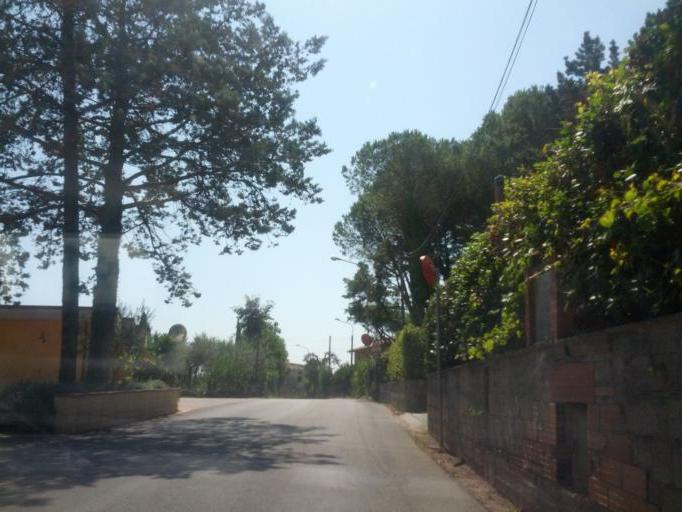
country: IT
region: Latium
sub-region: Provincia di Latina
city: Monte San Biagio
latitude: 41.3605
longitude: 13.3546
